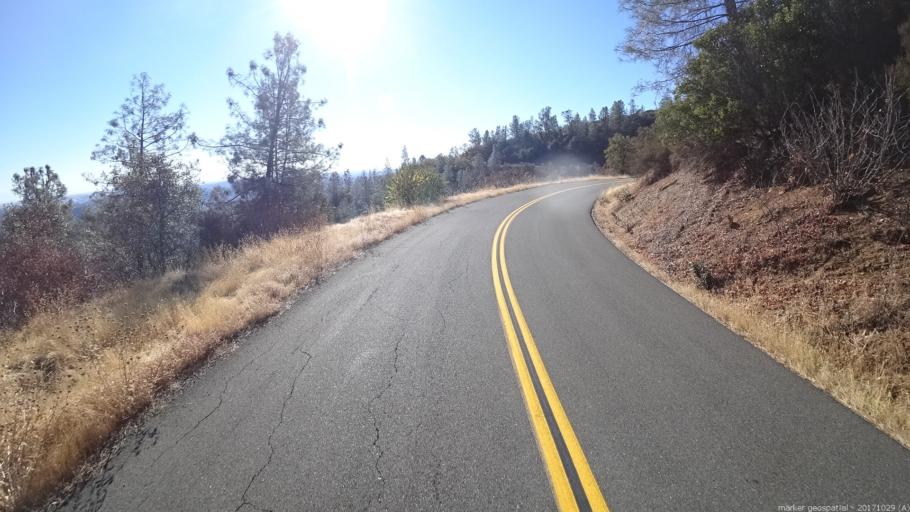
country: US
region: California
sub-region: Trinity County
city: Lewiston
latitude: 40.3807
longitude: -122.8456
